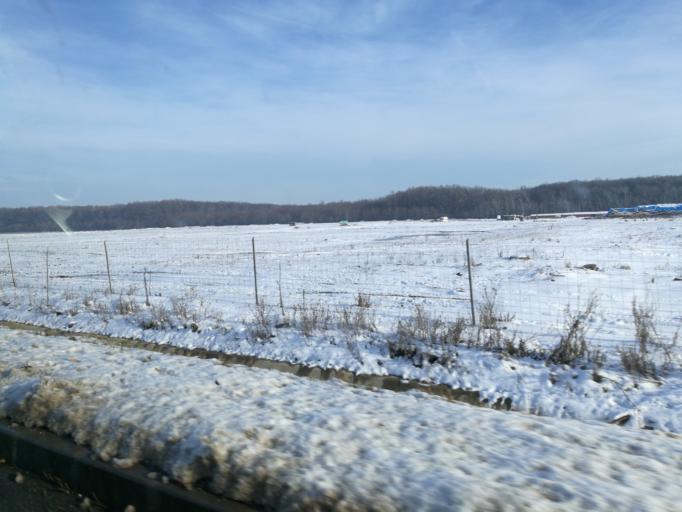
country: RO
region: Ilfov
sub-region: Voluntari City
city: Voluntari
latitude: 44.5099
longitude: 26.1640
